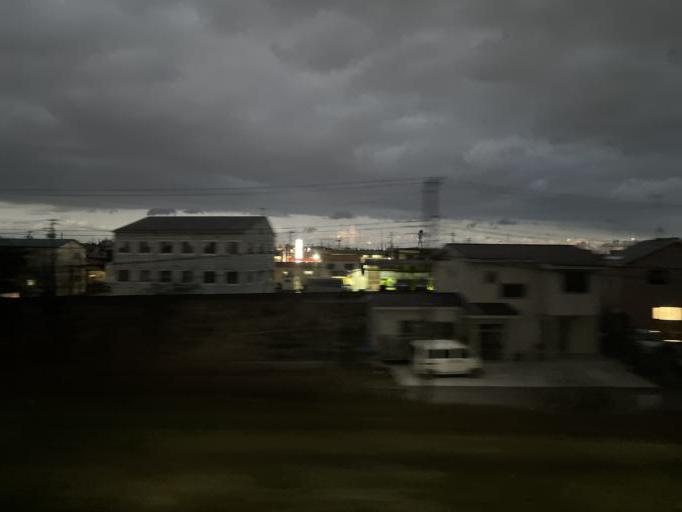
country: JP
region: Aomori
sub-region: Hachinohe Shi
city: Uchimaru
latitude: 40.5209
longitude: 141.4754
